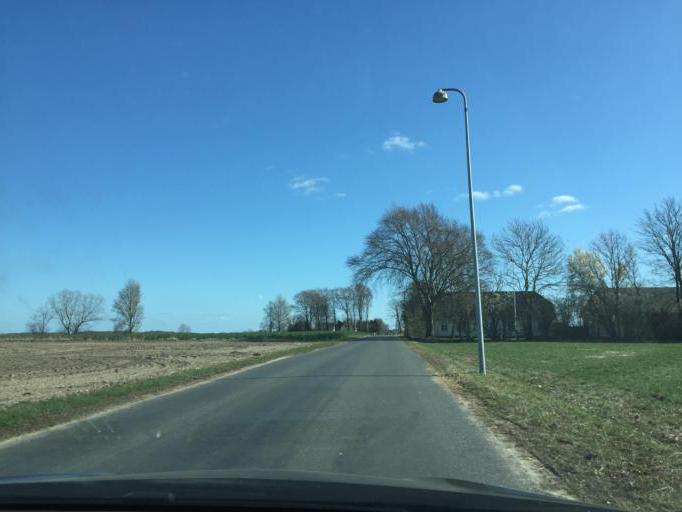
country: DK
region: South Denmark
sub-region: Kerteminde Kommune
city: Langeskov
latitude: 55.3397
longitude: 10.5237
